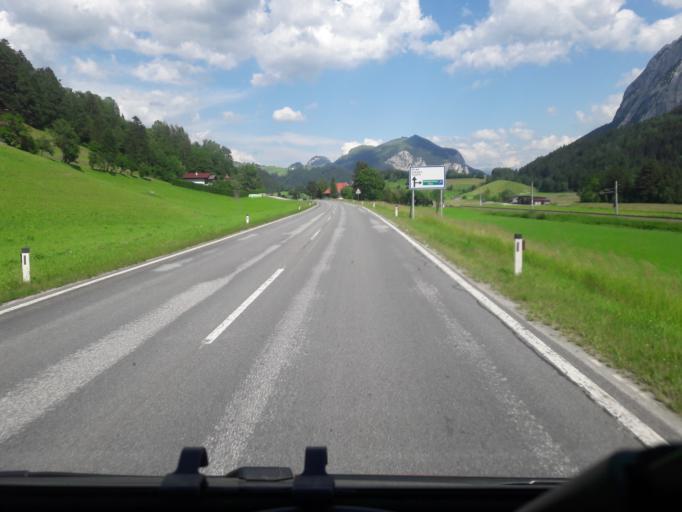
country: AT
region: Styria
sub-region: Politischer Bezirk Liezen
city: Tauplitz
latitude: 47.5524
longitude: 13.9860
